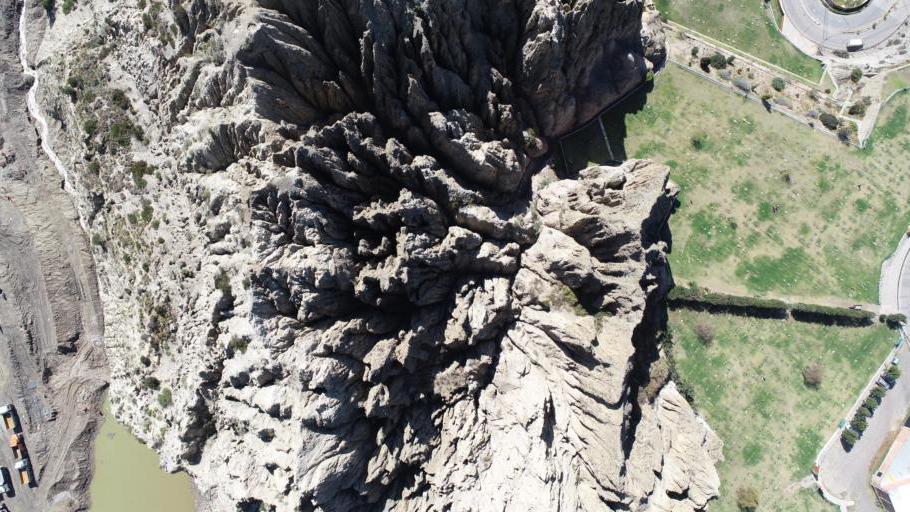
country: BO
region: La Paz
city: La Paz
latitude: -16.5207
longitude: -68.1205
